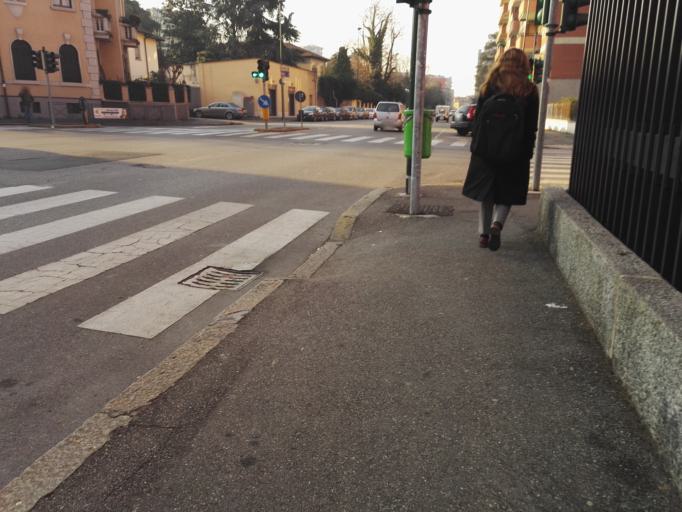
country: IT
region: Lombardy
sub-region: Citta metropolitana di Milano
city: Sesto San Giovanni
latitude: 45.5389
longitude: 9.2354
